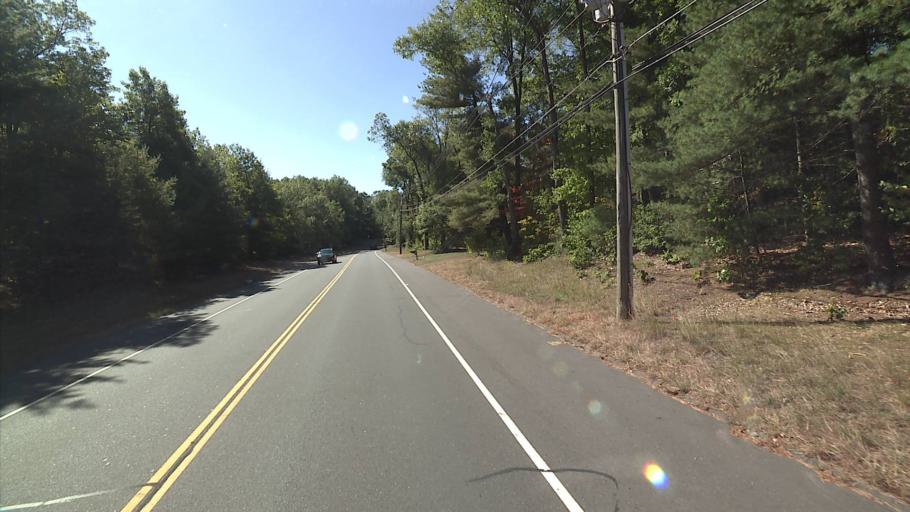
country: US
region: Connecticut
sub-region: Hartford County
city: Manchester
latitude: 41.7108
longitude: -72.5273
